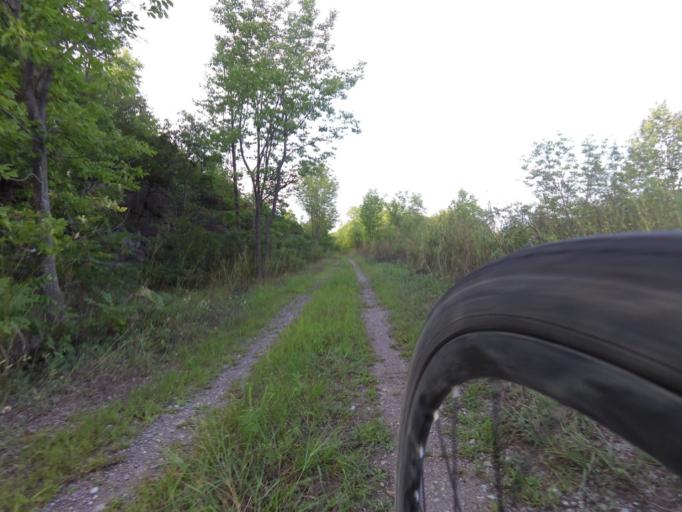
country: CA
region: Ontario
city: Kingston
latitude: 44.5313
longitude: -76.4066
